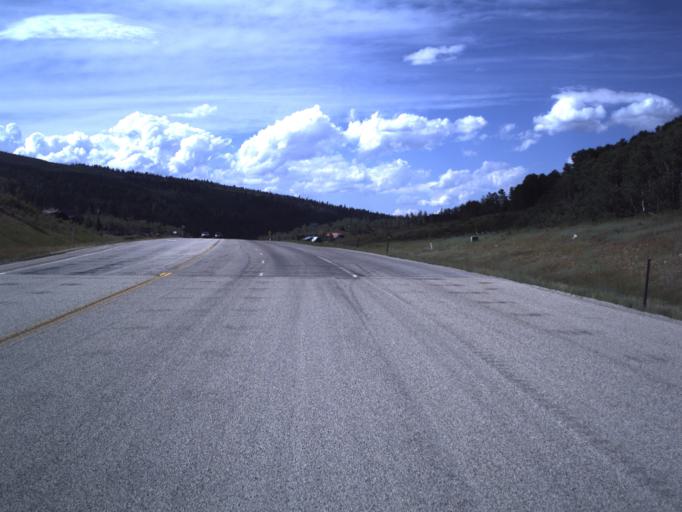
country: US
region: Utah
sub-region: Wasatch County
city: Heber
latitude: 40.2983
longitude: -111.2526
